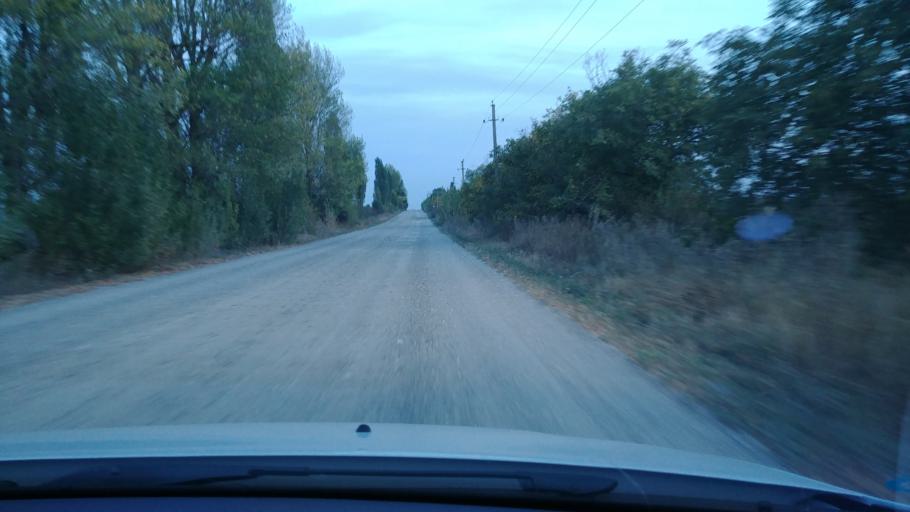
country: MD
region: Rezina
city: Saharna
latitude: 47.6719
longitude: 28.9392
